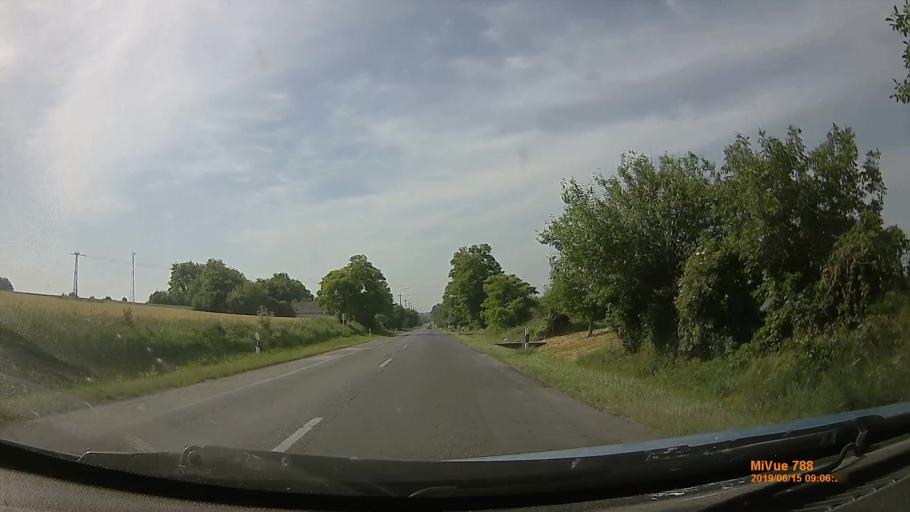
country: HU
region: Tolna
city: Iregszemcse
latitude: 46.7107
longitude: 18.1756
